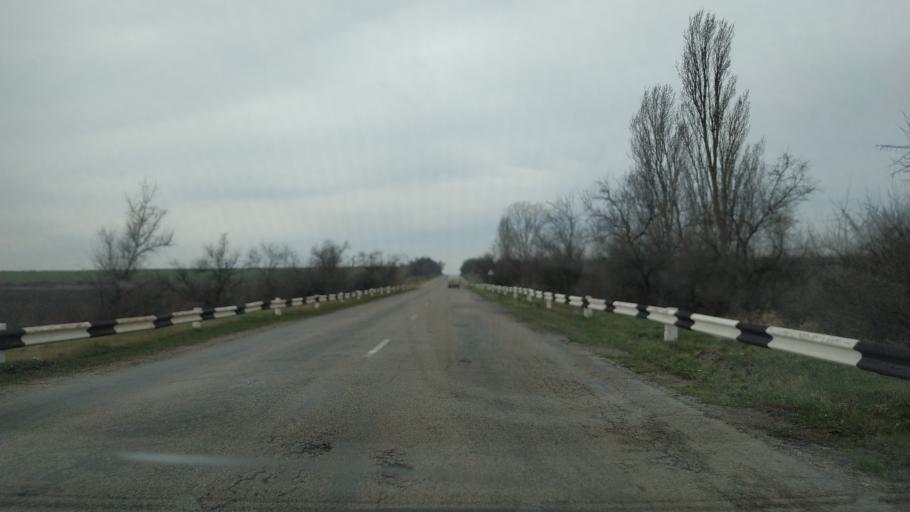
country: MD
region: Cahul
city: Cahul
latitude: 45.9589
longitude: 28.3784
